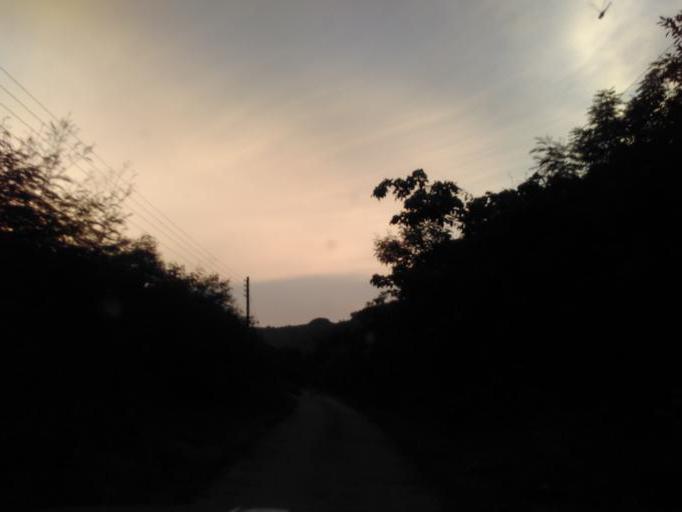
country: GH
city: Bekwai
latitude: 6.5160
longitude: -1.4413
